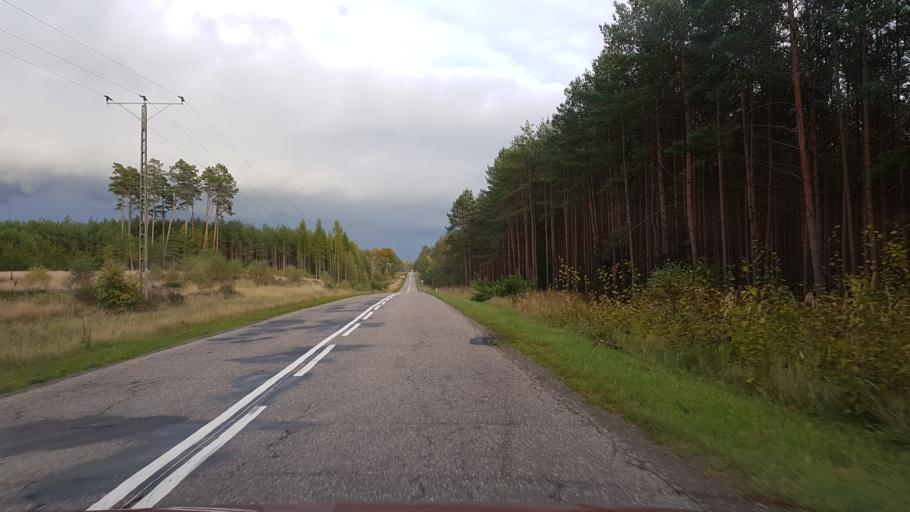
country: PL
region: West Pomeranian Voivodeship
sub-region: Powiat walecki
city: Tuczno
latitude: 53.1697
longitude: 16.2984
